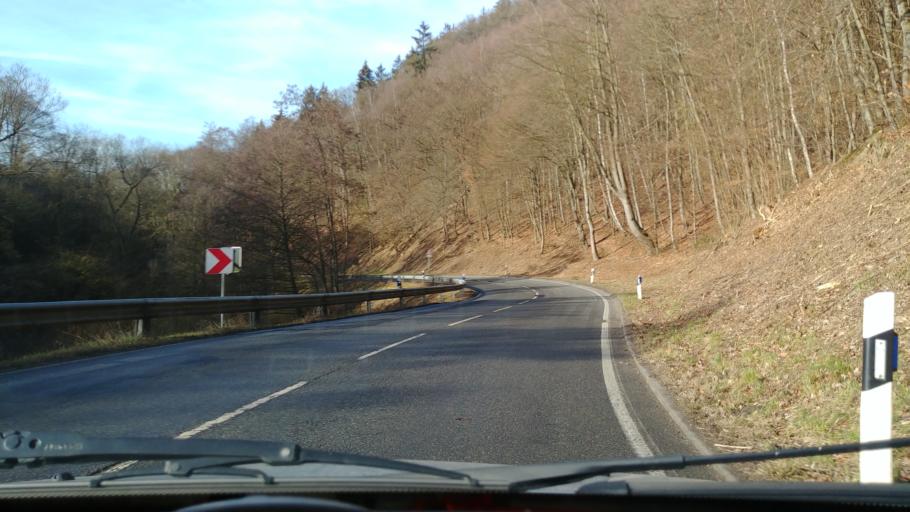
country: DE
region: Rheinland-Pfalz
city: Dachsenhausen
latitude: 50.2608
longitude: 7.6888
